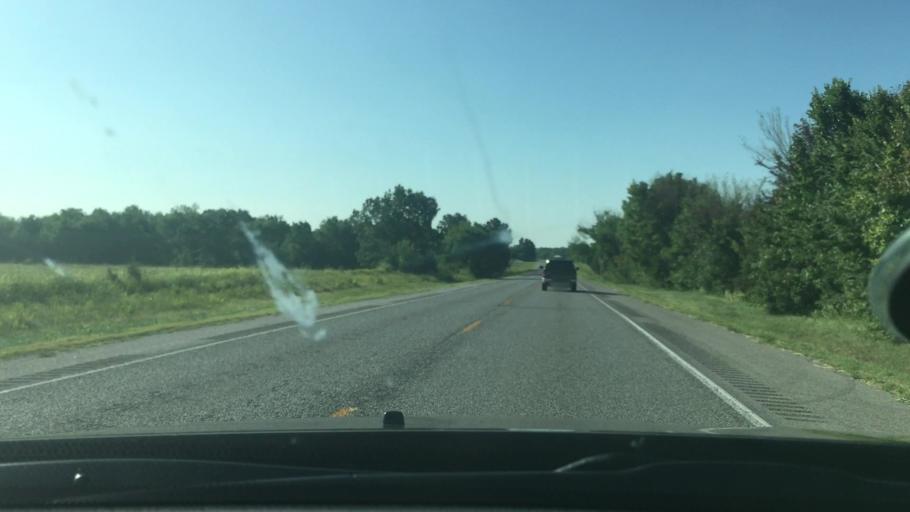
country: US
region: Oklahoma
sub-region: Johnston County
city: Tishomingo
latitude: 34.2533
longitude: -96.7625
